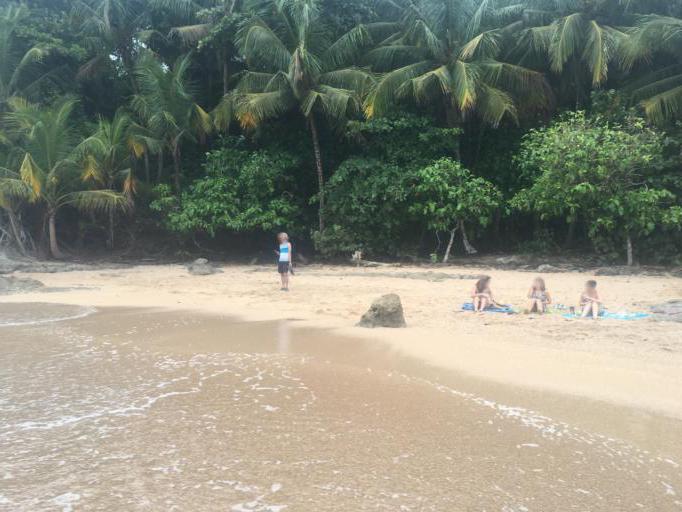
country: CR
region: Limon
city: Sixaola
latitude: 9.6400
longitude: -82.6484
